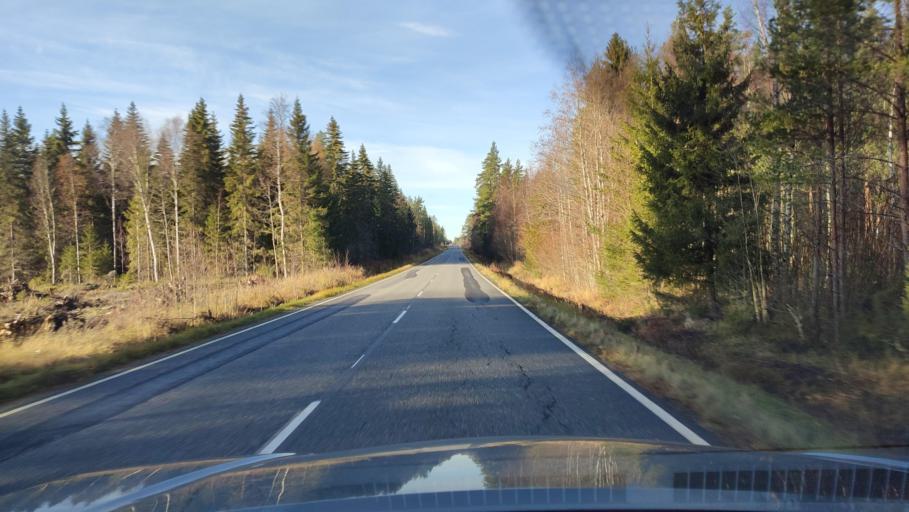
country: FI
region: Southern Ostrobothnia
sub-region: Suupohja
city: Teuva
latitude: 62.4606
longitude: 21.5450
